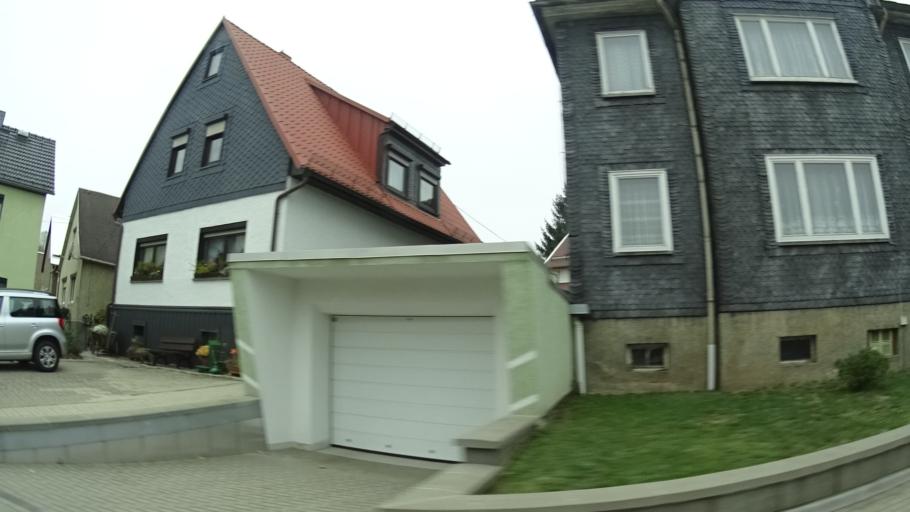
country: DE
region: Thuringia
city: Drobischau
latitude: 50.6305
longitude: 11.0731
